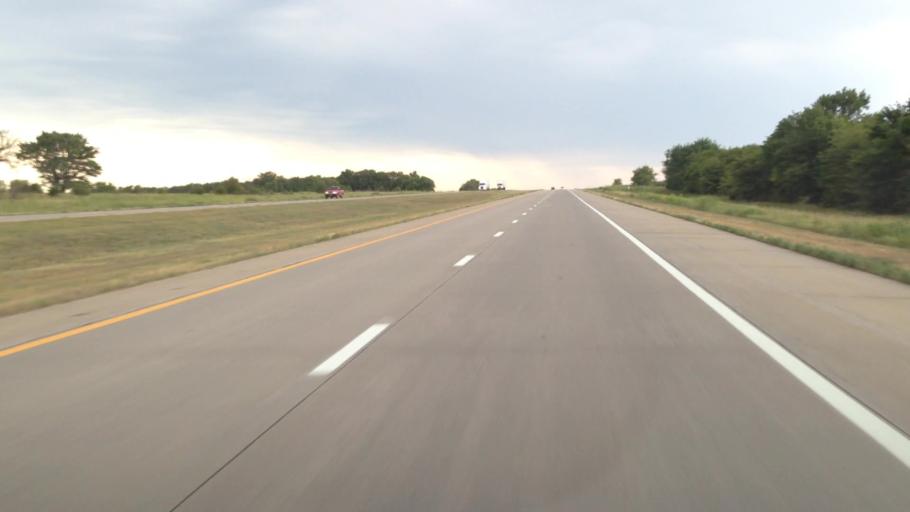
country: US
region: Kansas
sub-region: Osage County
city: Lyndon
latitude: 38.4696
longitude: -95.5324
